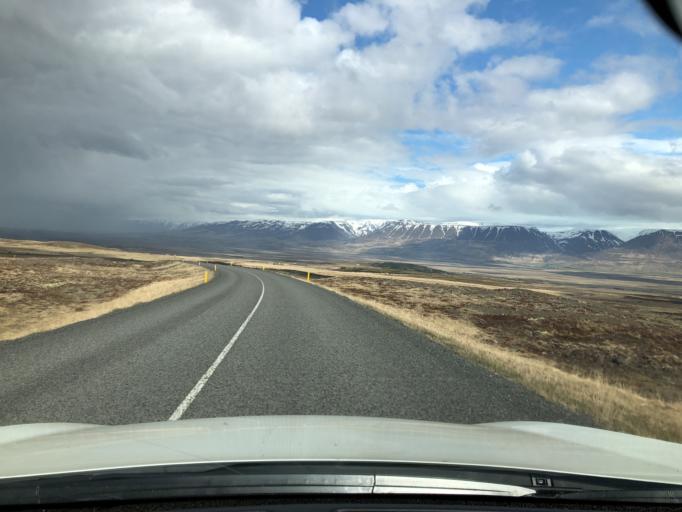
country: IS
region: Northwest
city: Saudarkrokur
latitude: 65.5309
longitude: -19.5145
